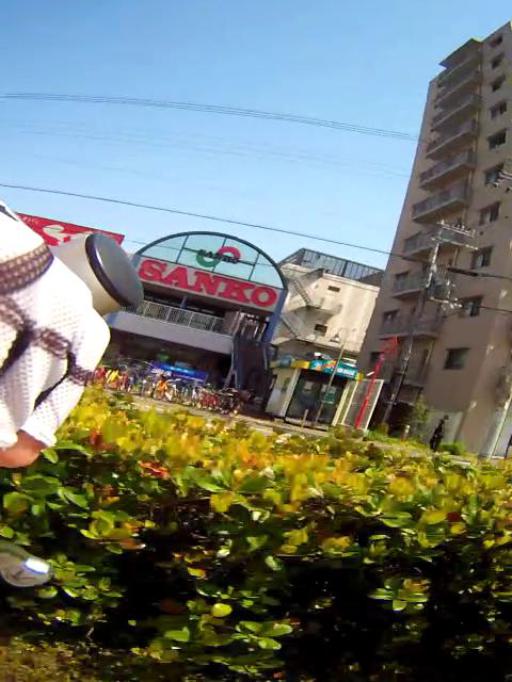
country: JP
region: Osaka
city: Yao
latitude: 34.6312
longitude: 135.5516
